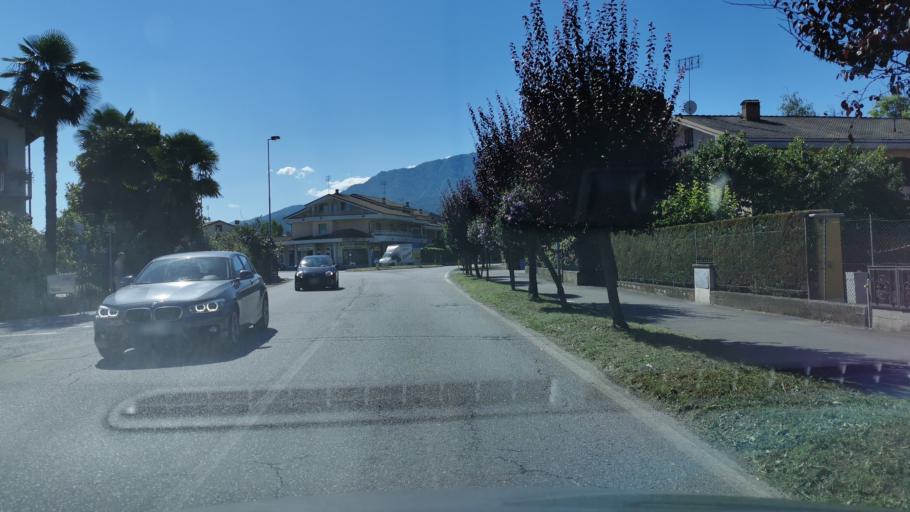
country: IT
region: Piedmont
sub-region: Provincia di Cuneo
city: Boves
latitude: 44.3348
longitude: 7.5447
